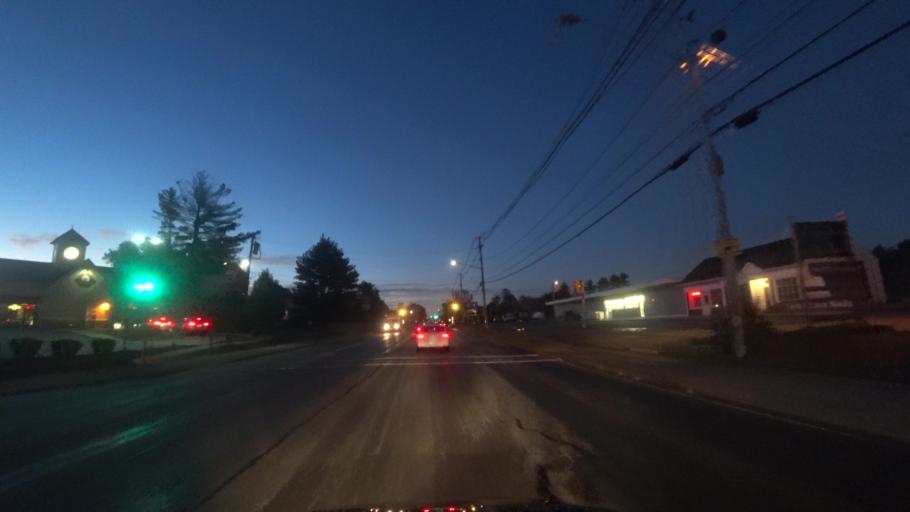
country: US
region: Massachusetts
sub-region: Middlesex County
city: North Reading
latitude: 42.5780
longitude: -71.1115
